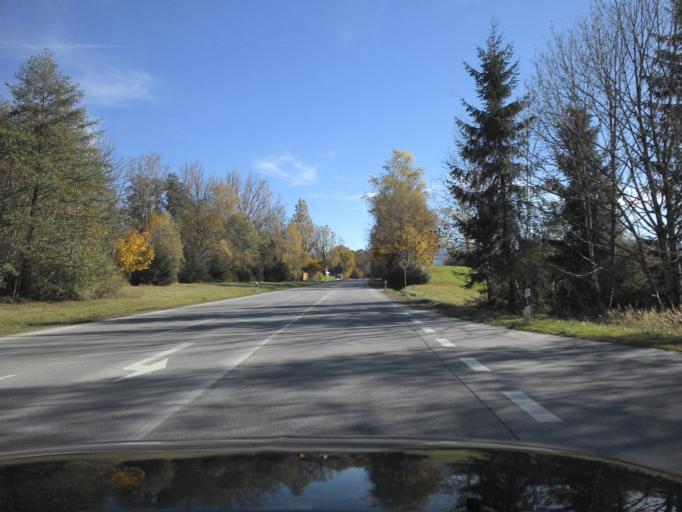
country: DE
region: Bavaria
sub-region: Upper Bavaria
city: Iffeldorf
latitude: 47.7720
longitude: 11.3418
